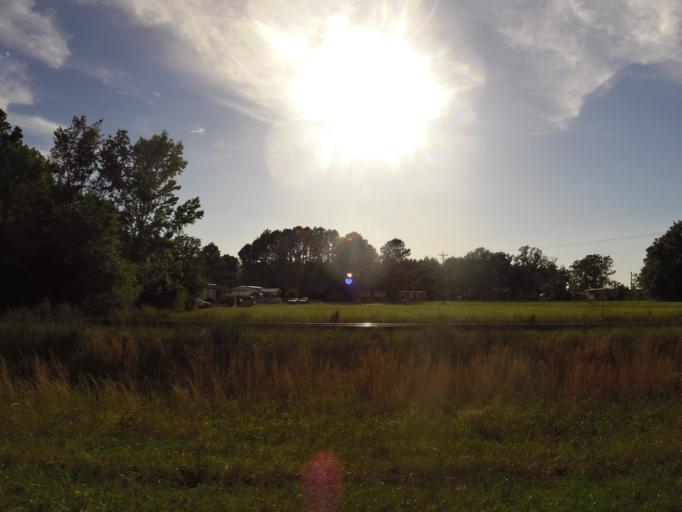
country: US
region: South Carolina
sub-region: Hampton County
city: Estill
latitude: 32.6701
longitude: -81.2434
